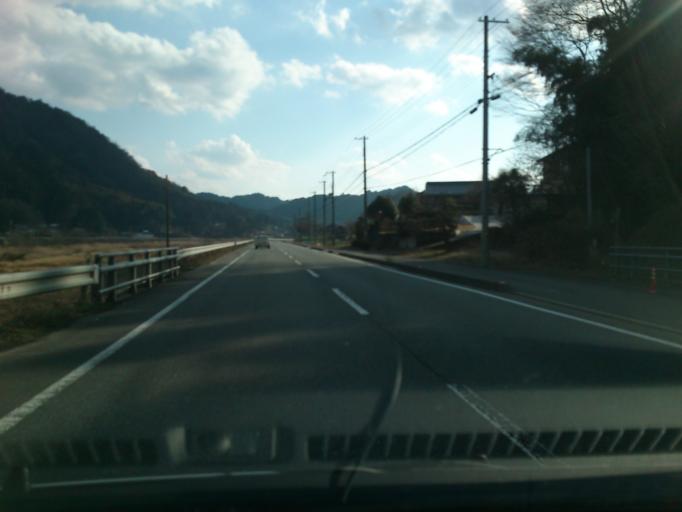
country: JP
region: Kyoto
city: Miyazu
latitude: 35.4172
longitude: 135.2027
